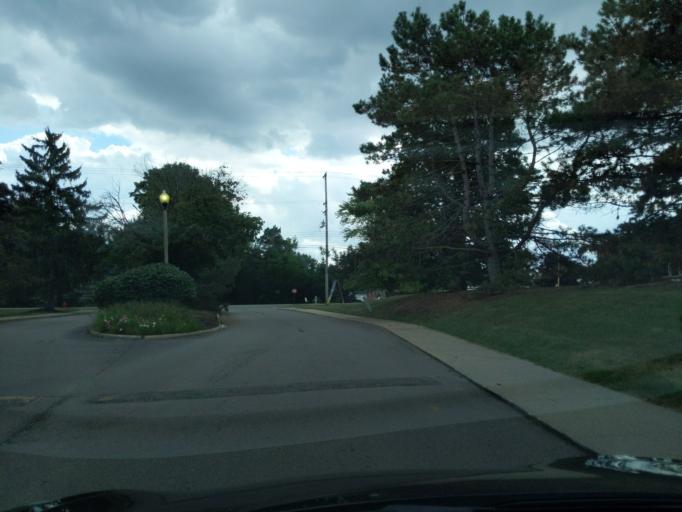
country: US
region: Michigan
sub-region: Ingham County
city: Holt
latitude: 42.6554
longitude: -84.5461
